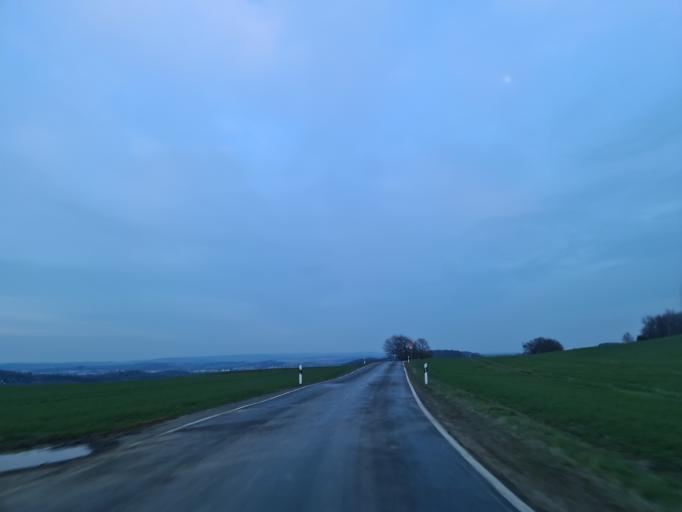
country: DE
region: Saxony
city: Bosenbrunn
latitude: 50.4199
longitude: 12.1128
